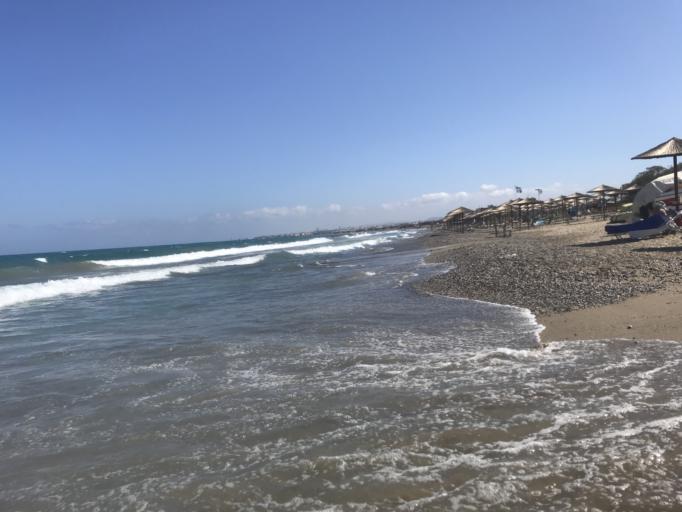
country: GR
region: Crete
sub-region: Nomos Irakleiou
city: Gazi
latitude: 35.3405
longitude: 25.0584
